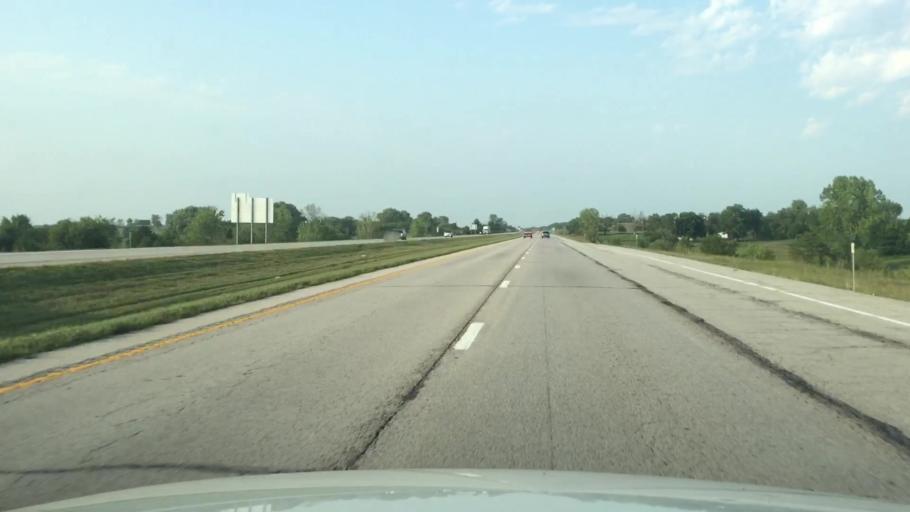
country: US
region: Missouri
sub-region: Harrison County
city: Bethany
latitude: 40.1581
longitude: -94.0305
